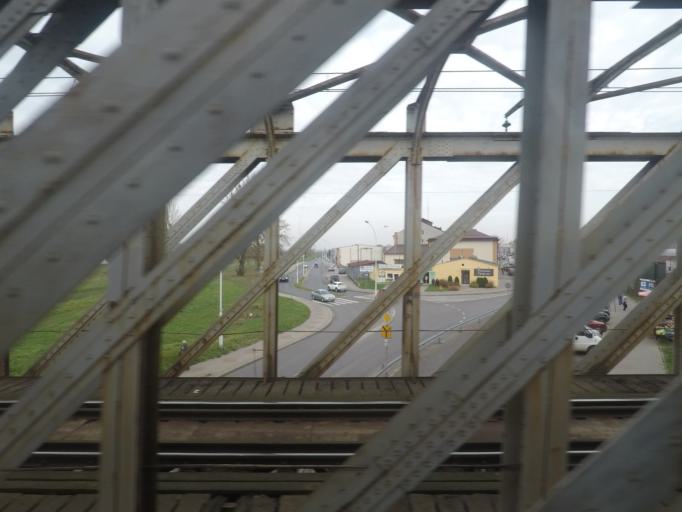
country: PL
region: Subcarpathian Voivodeship
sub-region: Przemysl
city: Przemysl
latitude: 49.7861
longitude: 22.7706
